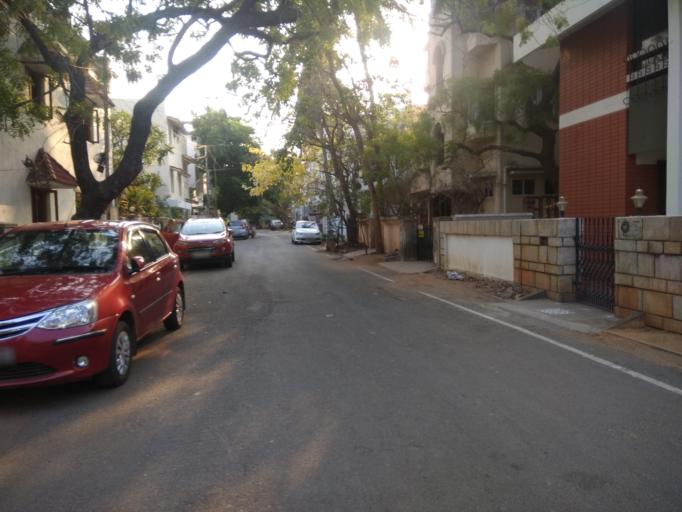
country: IN
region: Tamil Nadu
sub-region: Chennai
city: Gandhi Nagar
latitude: 13.0204
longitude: 80.2439
